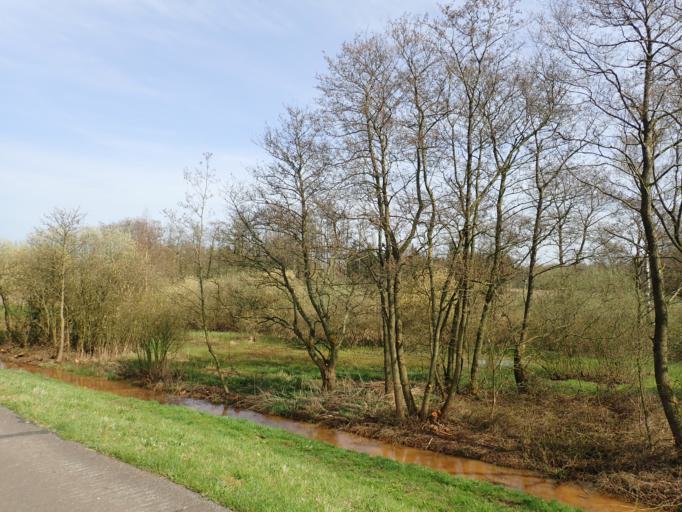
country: BE
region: Flanders
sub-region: Provincie Antwerpen
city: Lier
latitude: 51.1534
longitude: 4.5965
